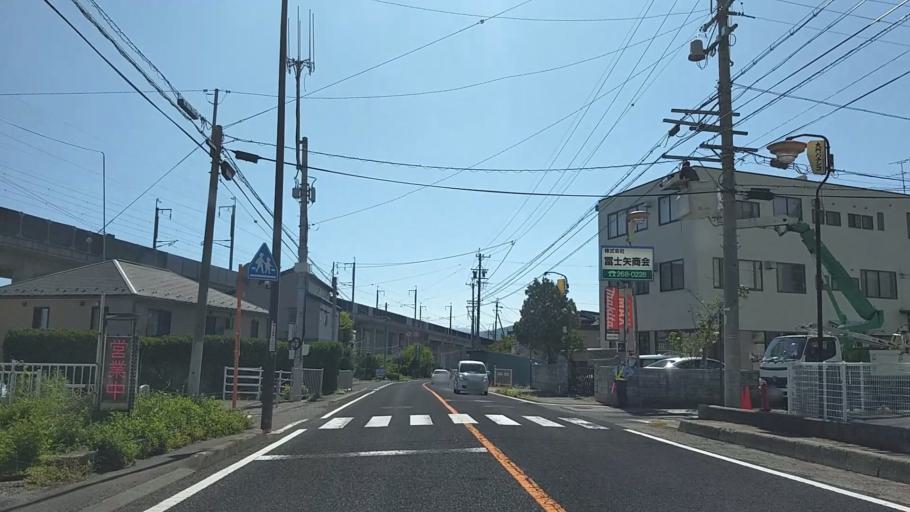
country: JP
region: Nagano
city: Nagano-shi
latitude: 36.6345
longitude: 138.1686
